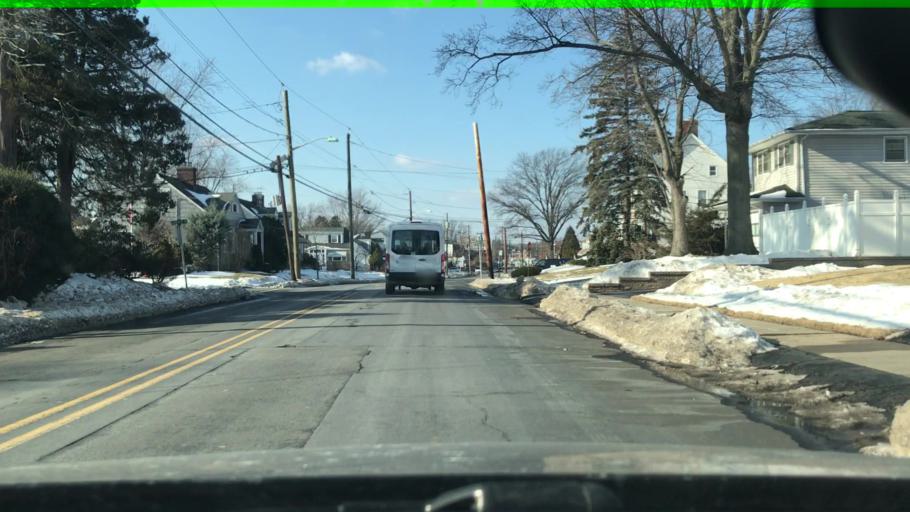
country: US
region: New Jersey
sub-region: Union County
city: Union
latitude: 40.6971
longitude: -74.2792
